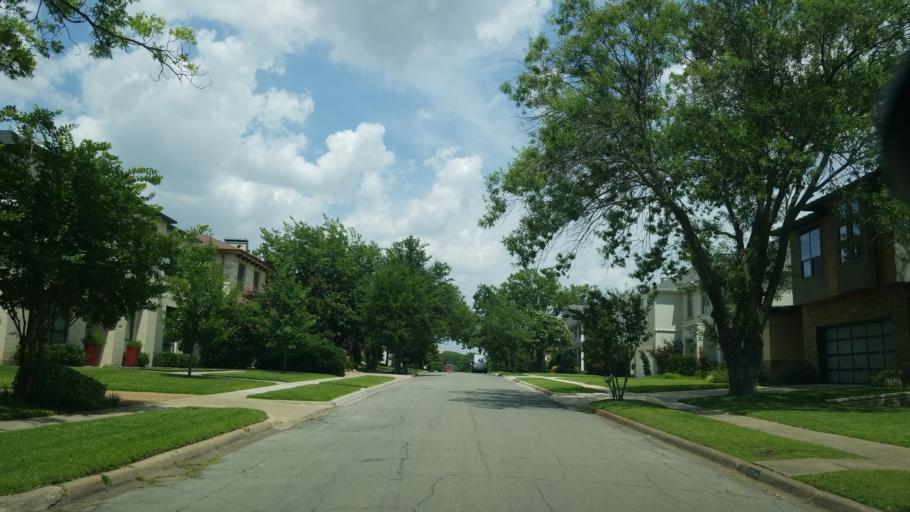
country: US
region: Texas
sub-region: Dallas County
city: University Park
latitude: 32.8696
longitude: -96.7893
